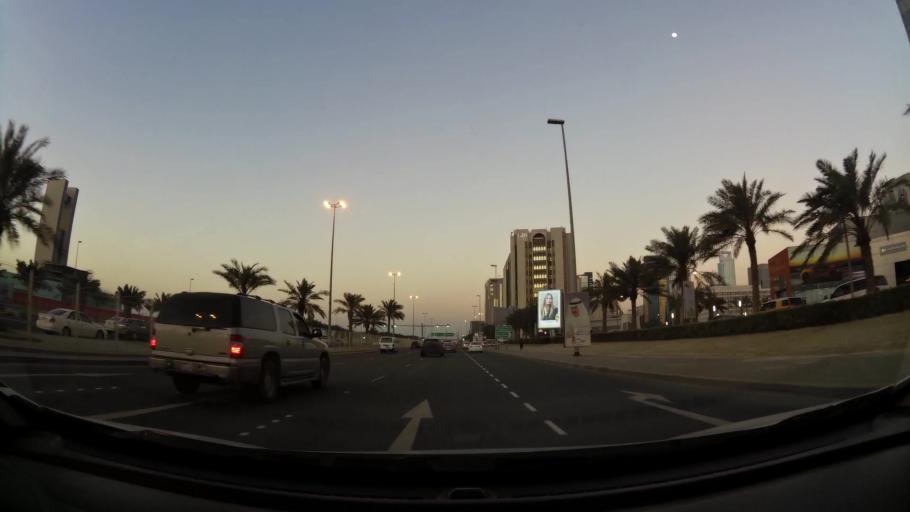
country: BH
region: Manama
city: Manama
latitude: 26.2403
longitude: 50.5816
